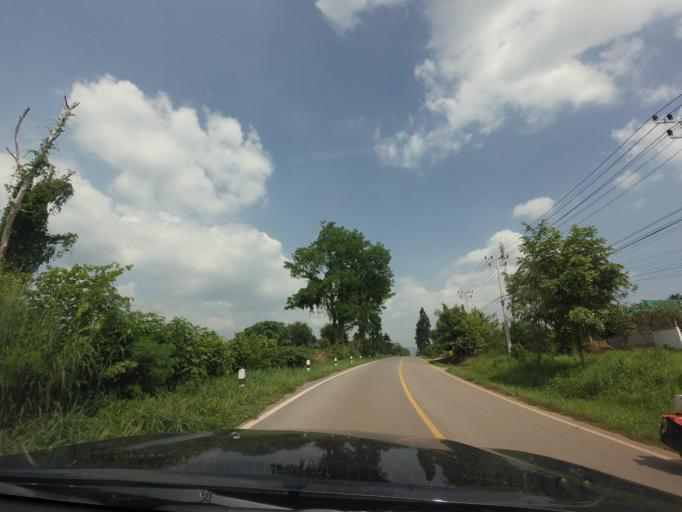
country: TH
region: Uttaradit
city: Ban Khok
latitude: 18.0203
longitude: 101.0513
